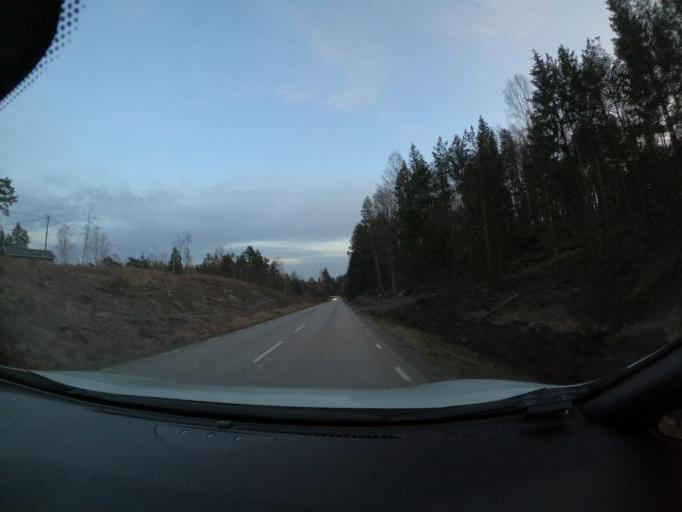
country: SE
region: Vaestra Goetaland
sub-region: Harryda Kommun
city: Molnlycke
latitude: 57.6463
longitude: 12.1597
